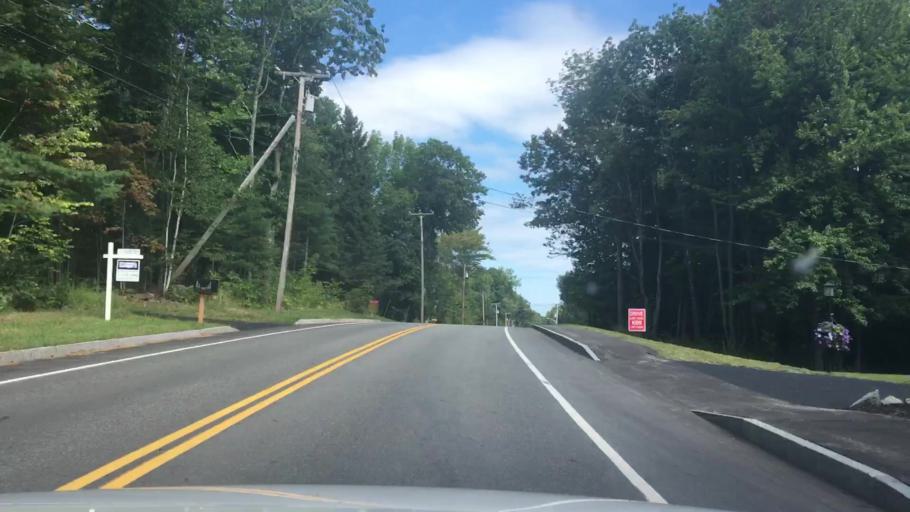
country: US
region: Maine
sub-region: Androscoggin County
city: Auburn
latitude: 44.1112
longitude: -70.2503
